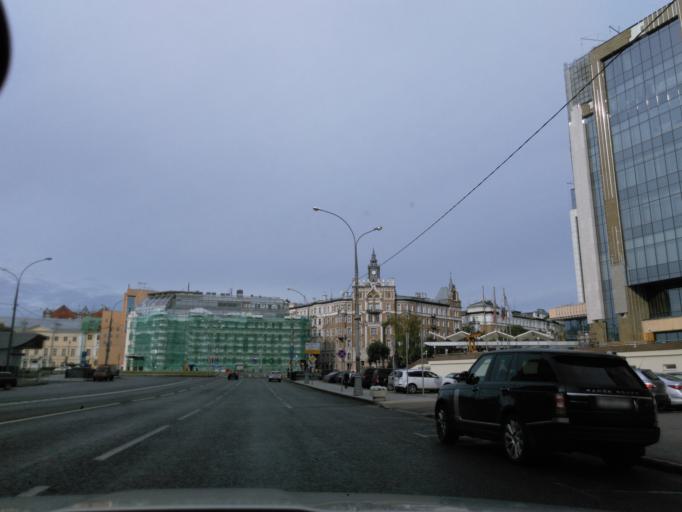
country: RU
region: Moscow
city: Moscow
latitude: 55.7669
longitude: 37.6379
